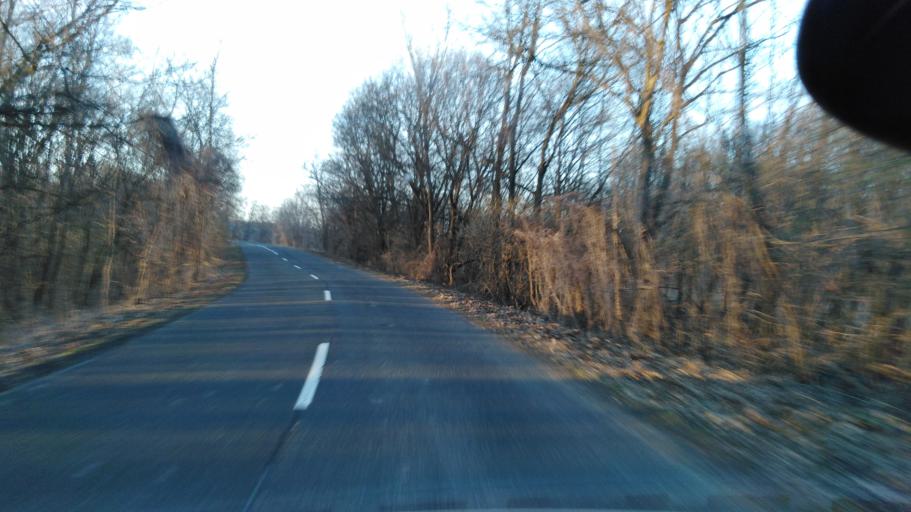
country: HU
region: Nograd
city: Salgotarjan
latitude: 48.0711
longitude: 19.8167
